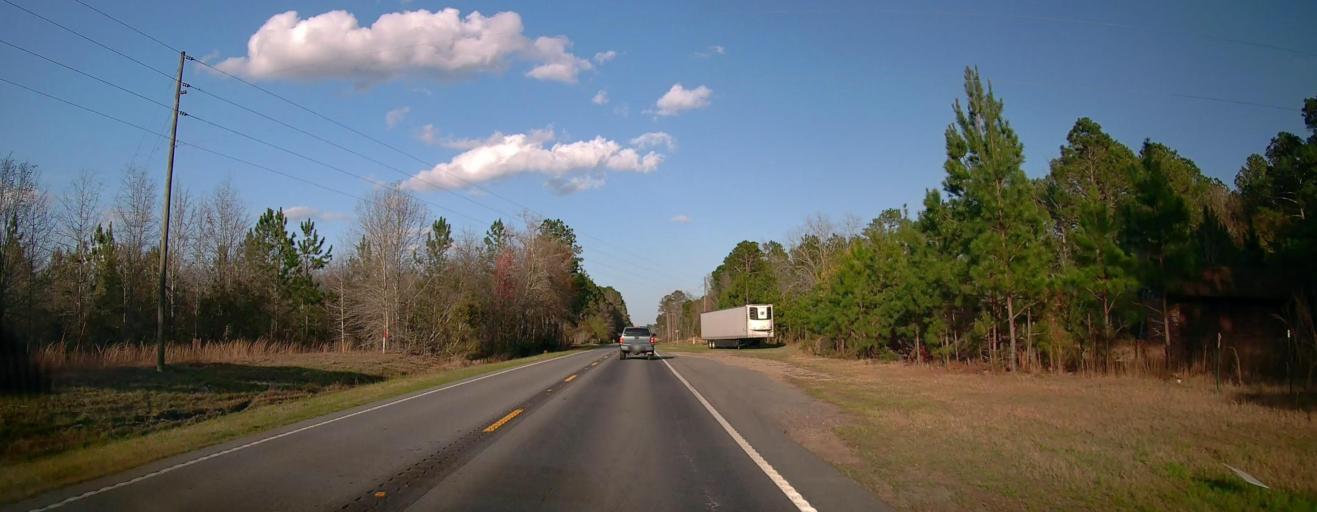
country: US
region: Georgia
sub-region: Tattnall County
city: Reidsville
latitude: 32.1361
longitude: -82.0412
